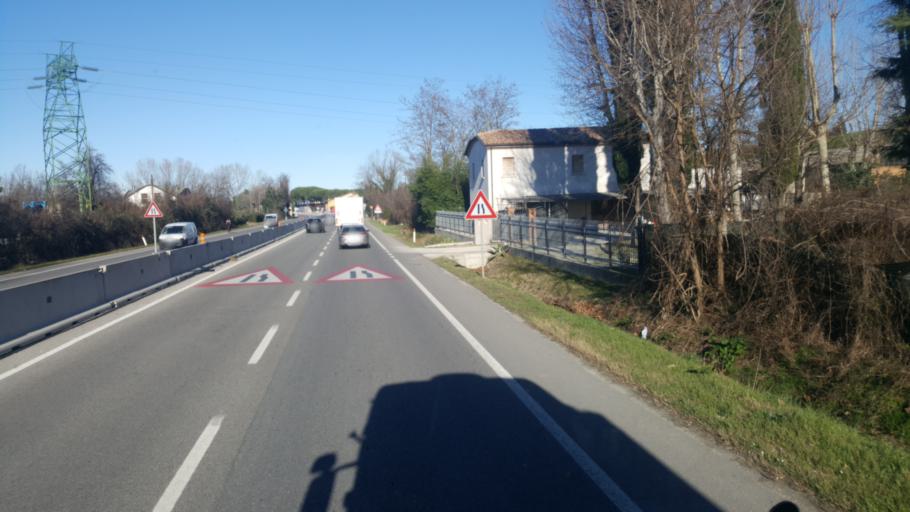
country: IT
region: Emilia-Romagna
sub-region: Provincia di Rimini
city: Cerasolo
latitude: 43.9966
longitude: 12.5400
